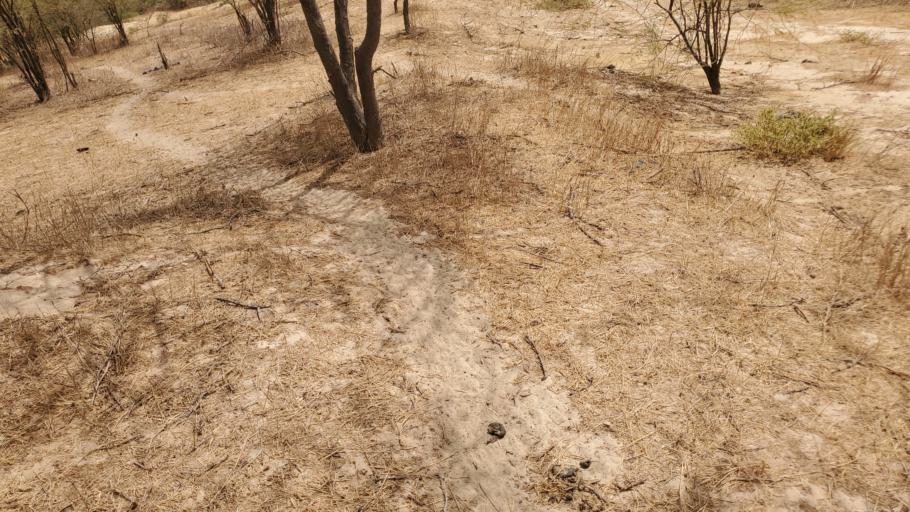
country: SN
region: Saint-Louis
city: Saint-Louis
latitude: 15.9524
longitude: -16.4327
